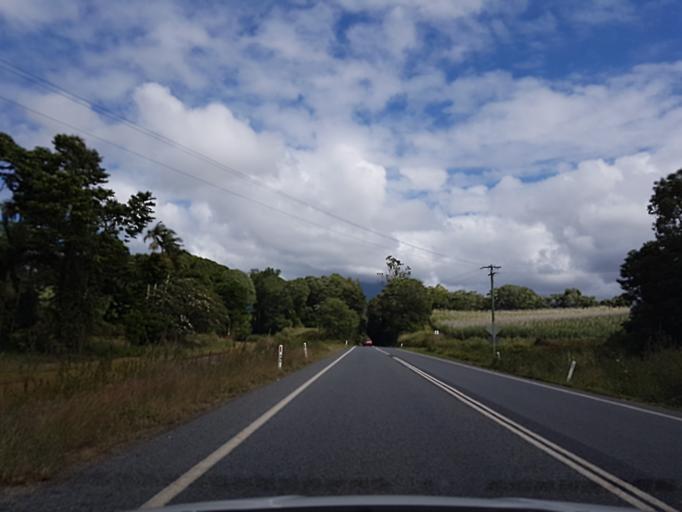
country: AU
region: Queensland
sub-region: Cairns
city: Port Douglas
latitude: -16.4779
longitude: 145.3980
